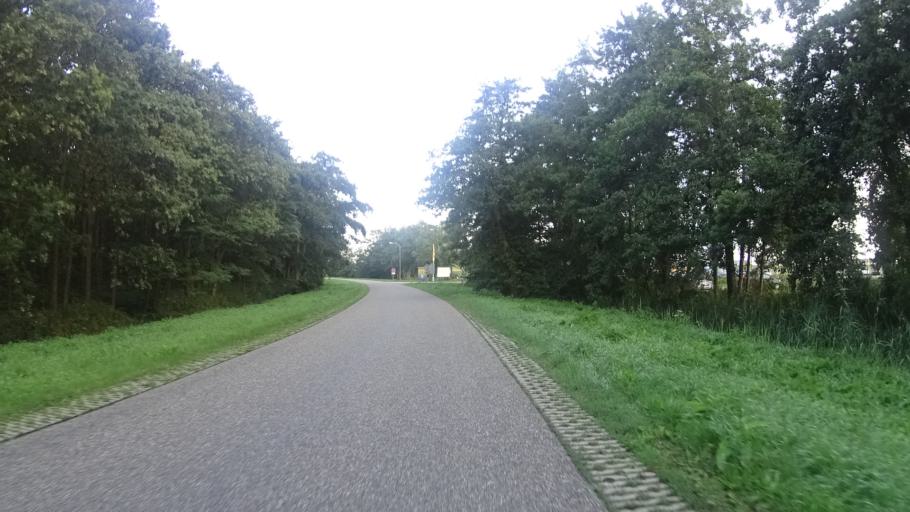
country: NL
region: North Holland
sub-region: Gemeente Hollands Kroon
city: Den Oever
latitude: 52.9224
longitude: 5.0479
